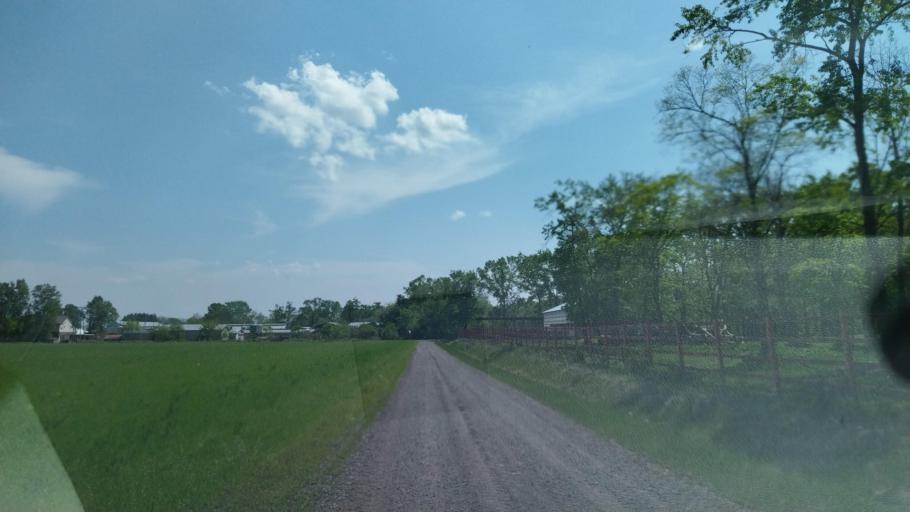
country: JP
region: Hokkaido
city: Otofuke
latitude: 43.1339
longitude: 143.2183
